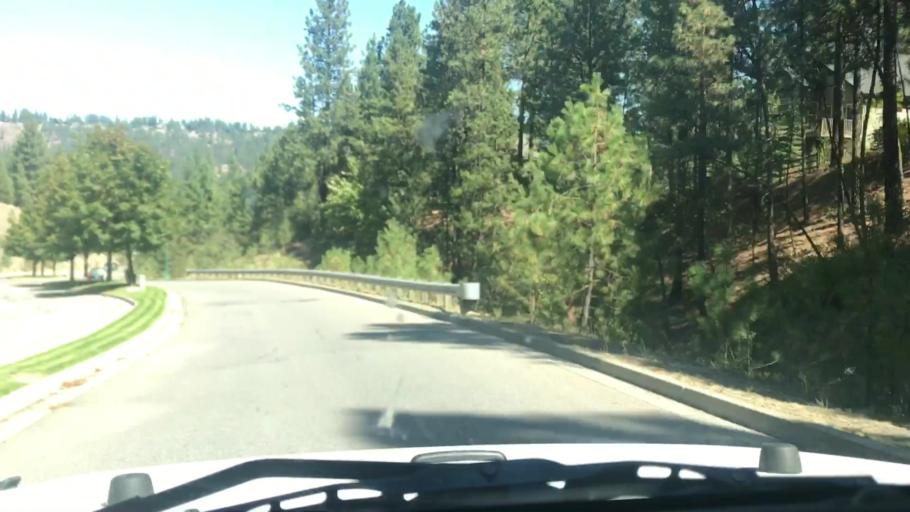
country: US
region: Washington
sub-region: Spokane County
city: Spokane
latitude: 47.5957
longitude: -117.4161
